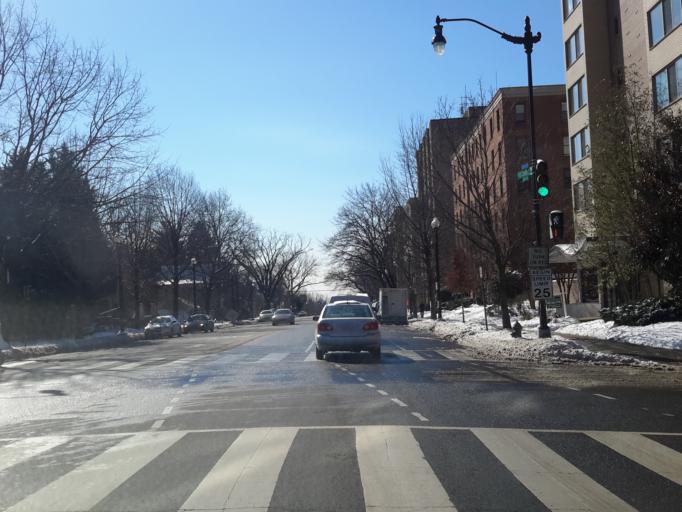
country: US
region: Maryland
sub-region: Montgomery County
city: Friendship Village
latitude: 38.9277
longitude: -77.0732
